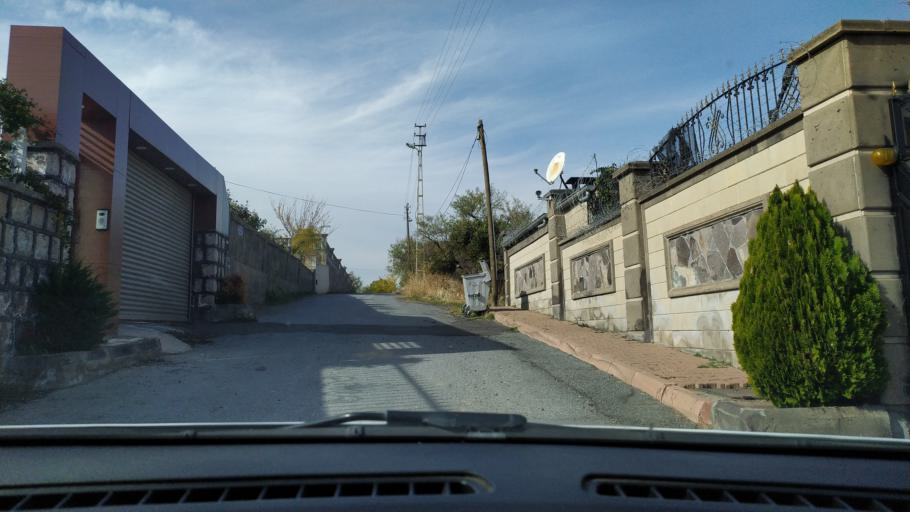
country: TR
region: Kayseri
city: Kayseri
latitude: 38.6799
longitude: 35.4905
